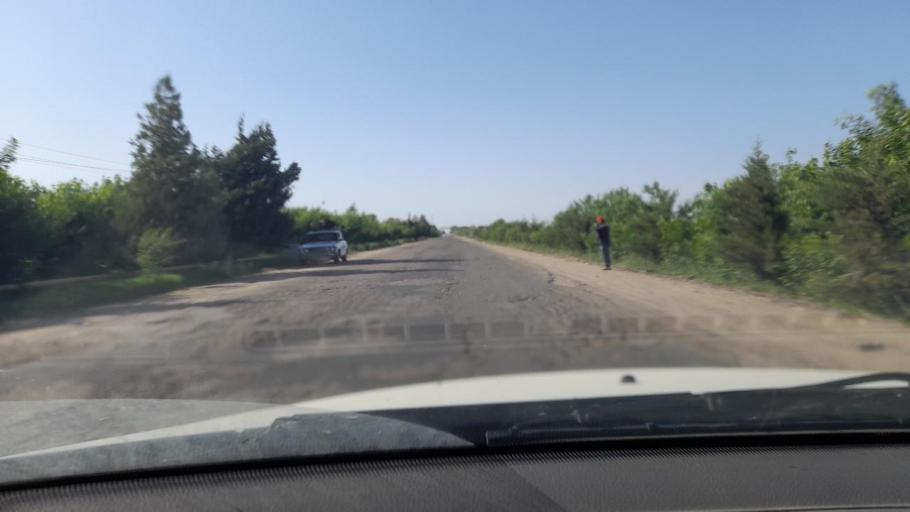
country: UZ
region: Bukhara
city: Romiton
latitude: 40.0703
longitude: 64.3267
